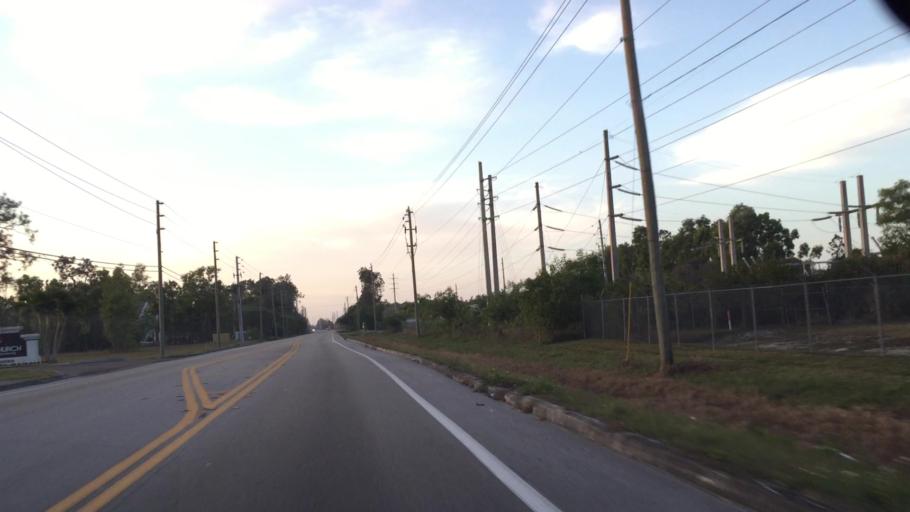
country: US
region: Florida
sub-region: Lee County
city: Villas
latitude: 26.5723
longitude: -81.8472
